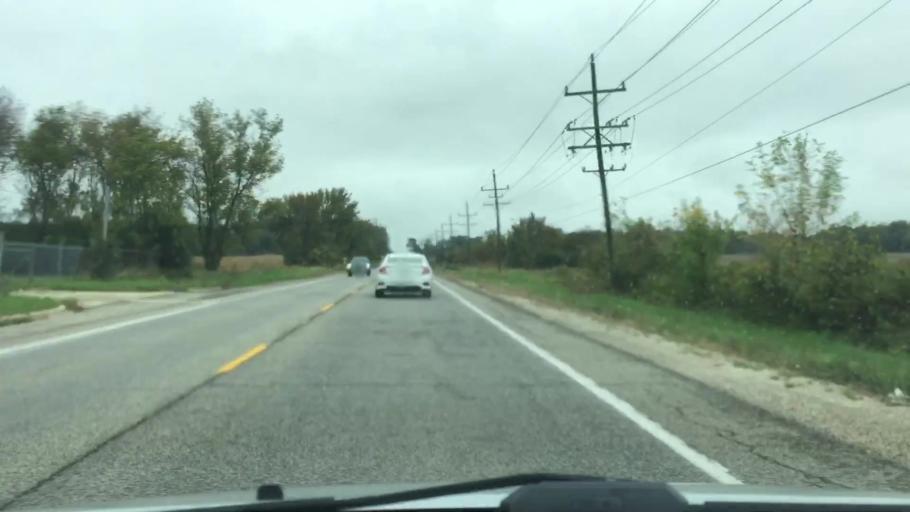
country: US
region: Illinois
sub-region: McHenry County
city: Prairie Grove
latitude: 42.2914
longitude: -88.2870
